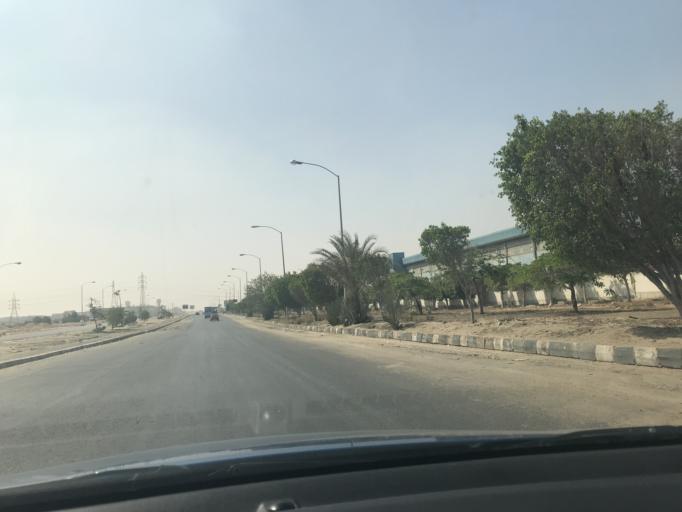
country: EG
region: Eastern Province
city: Bilbays
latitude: 30.2506
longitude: 31.7589
